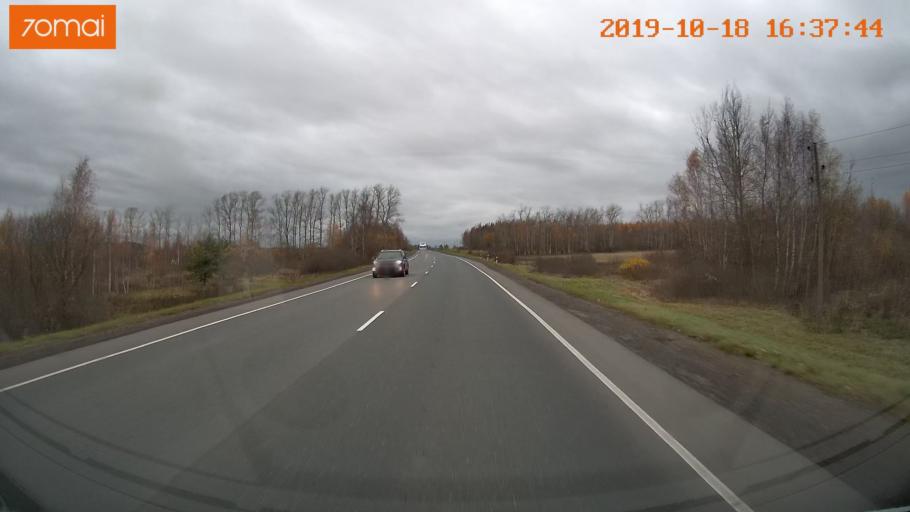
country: RU
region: Vladimir
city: Suzdal'
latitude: 56.4260
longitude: 40.4756
